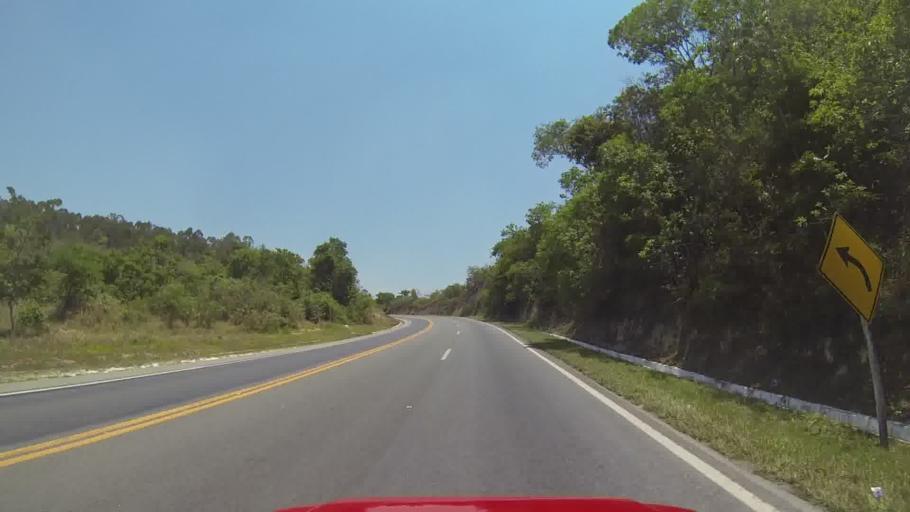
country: BR
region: Minas Gerais
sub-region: Itapecerica
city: Itapecerica
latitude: -20.2984
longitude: -45.1944
